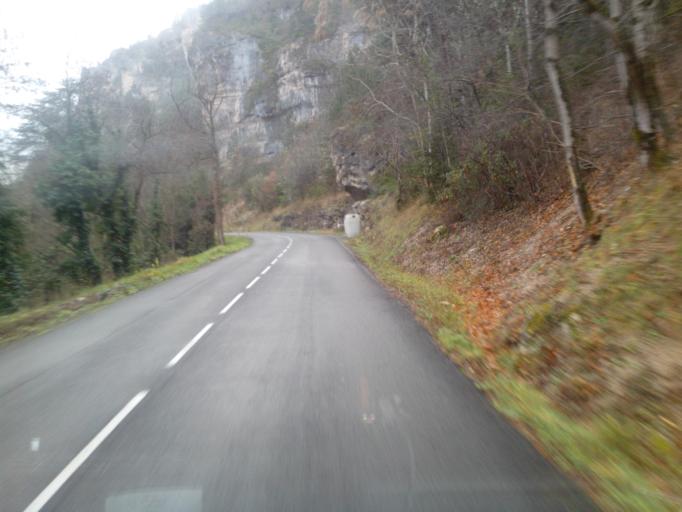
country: FR
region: Languedoc-Roussillon
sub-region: Departement de la Lozere
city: Chanac
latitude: 44.3350
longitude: 3.3574
